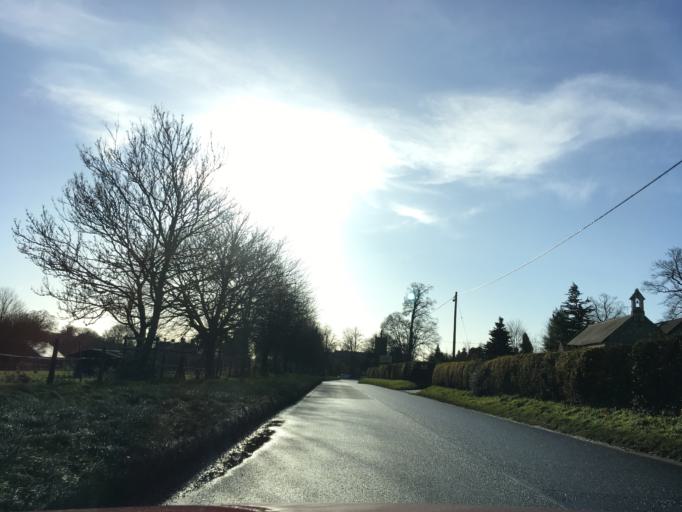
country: GB
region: England
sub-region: Wiltshire
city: Collingbourne Kingston
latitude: 51.3037
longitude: -1.6584
